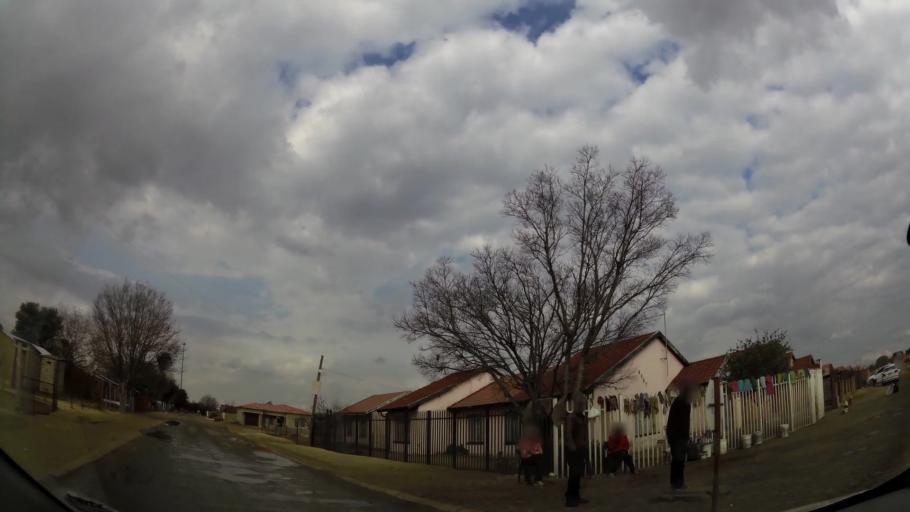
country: ZA
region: Orange Free State
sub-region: Fezile Dabi District Municipality
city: Sasolburg
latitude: -26.8469
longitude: 27.8592
